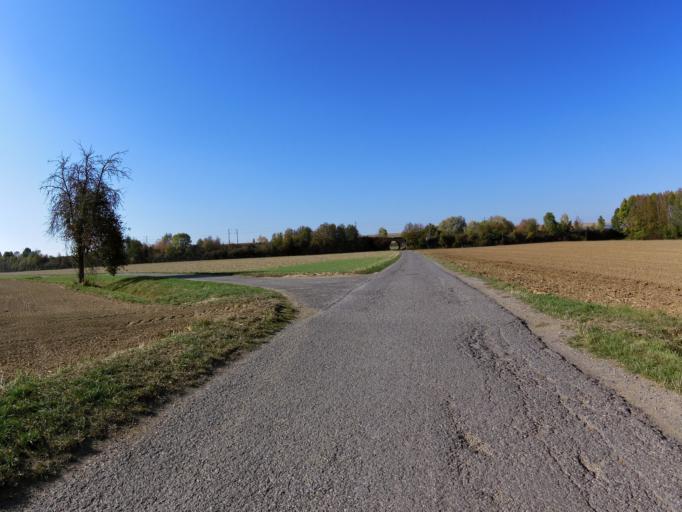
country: DE
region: Bavaria
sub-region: Regierungsbezirk Unterfranken
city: Geroldshausen
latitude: 49.6972
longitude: 9.9244
